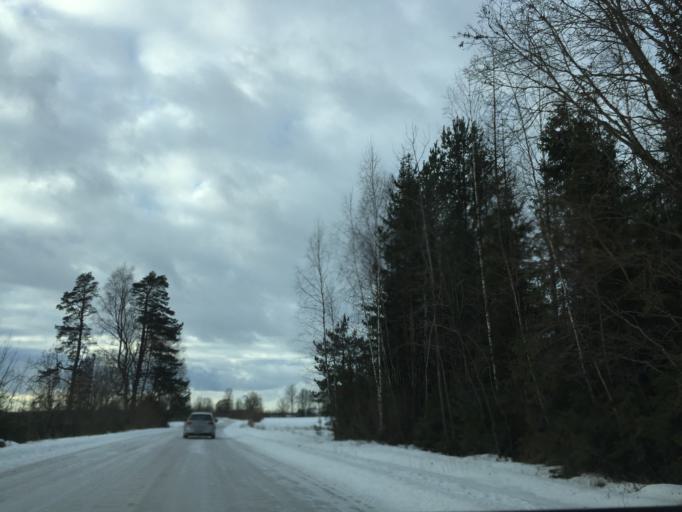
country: LV
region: Lielvarde
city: Lielvarde
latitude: 56.6177
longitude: 24.7726
